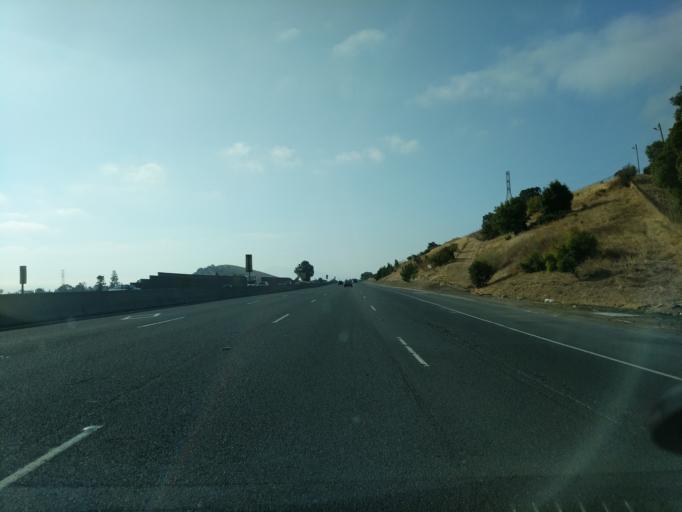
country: US
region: California
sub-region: Contra Costa County
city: Vine Hill
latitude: 38.0182
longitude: -122.0957
